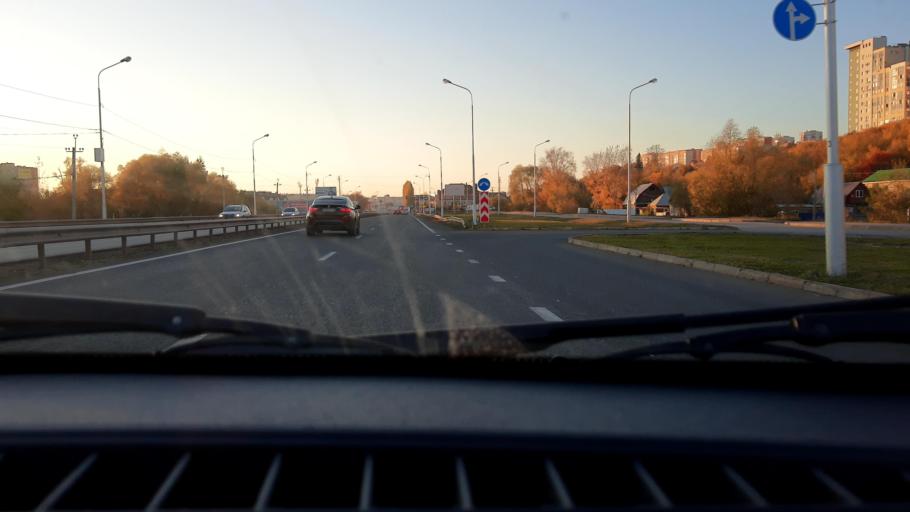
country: RU
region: Bashkortostan
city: Ufa
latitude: 54.6858
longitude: 55.9922
